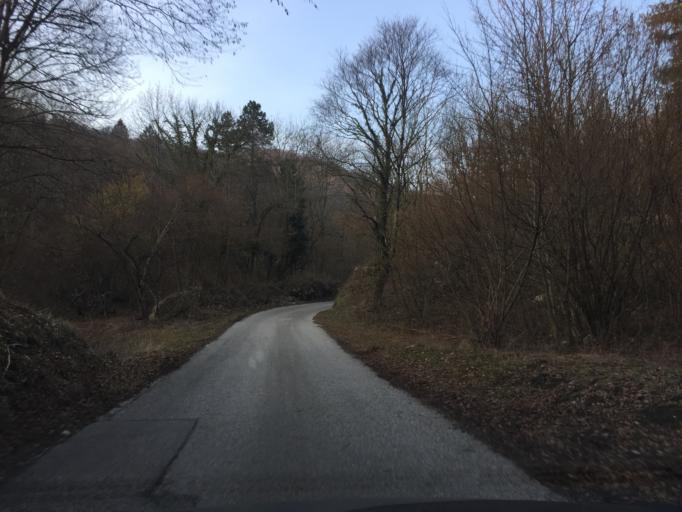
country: SI
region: Kanal
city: Kanal
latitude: 46.0557
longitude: 13.6662
